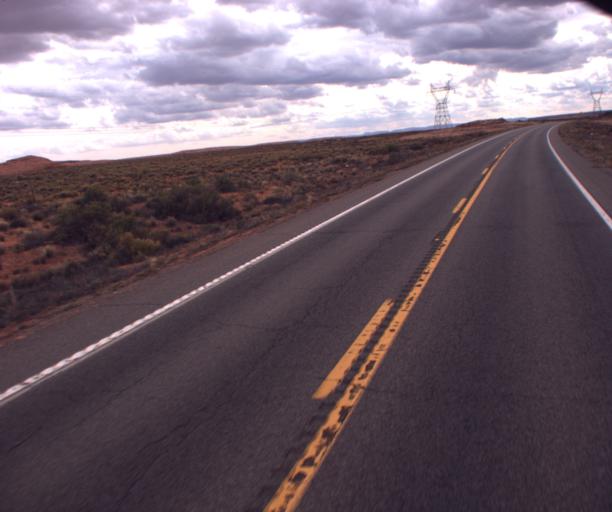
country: US
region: Arizona
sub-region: Navajo County
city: Kayenta
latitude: 36.8517
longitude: -109.8315
